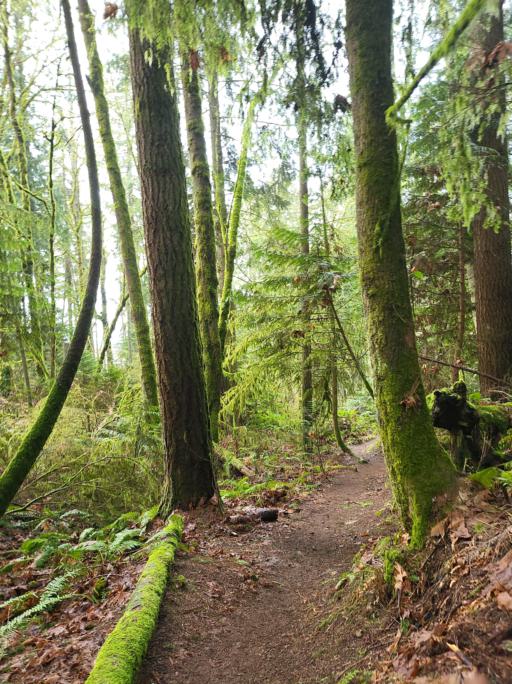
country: US
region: Washington
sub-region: King County
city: Newcastle
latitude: 47.5256
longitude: -122.1419
